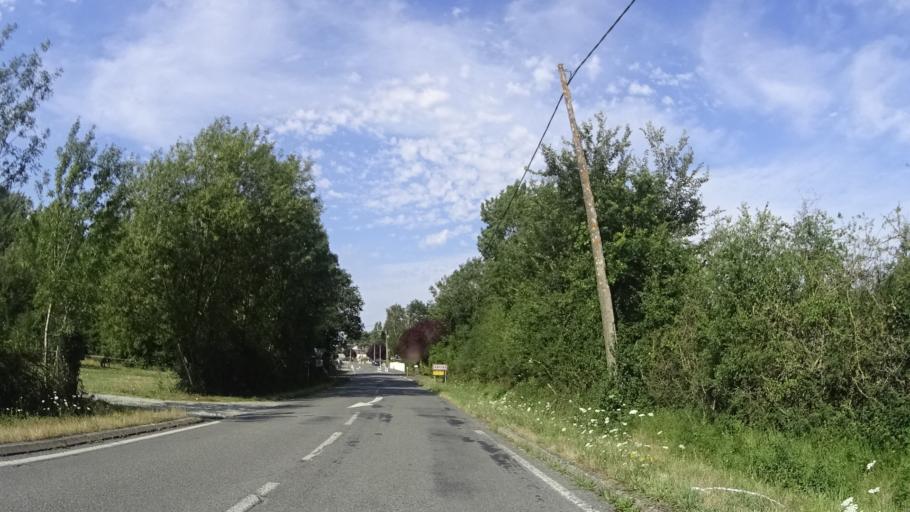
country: FR
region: Pays de la Loire
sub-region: Departement de la Loire-Atlantique
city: Saffre
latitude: 47.5039
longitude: -1.5707
